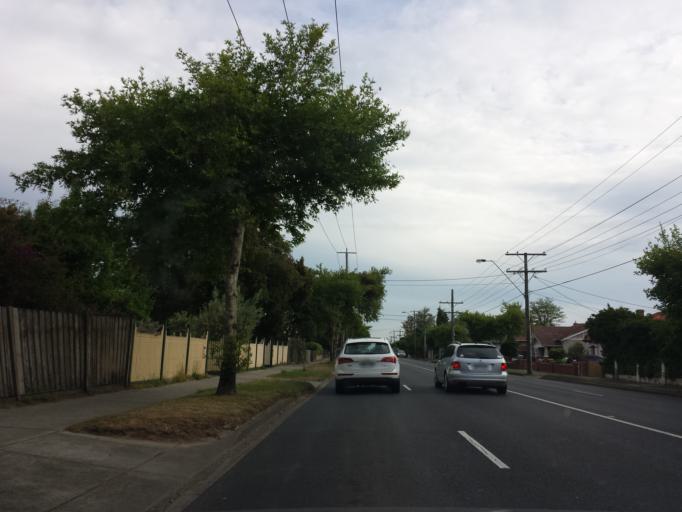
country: AU
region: Victoria
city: Hughesdale
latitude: -37.9042
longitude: 145.0861
